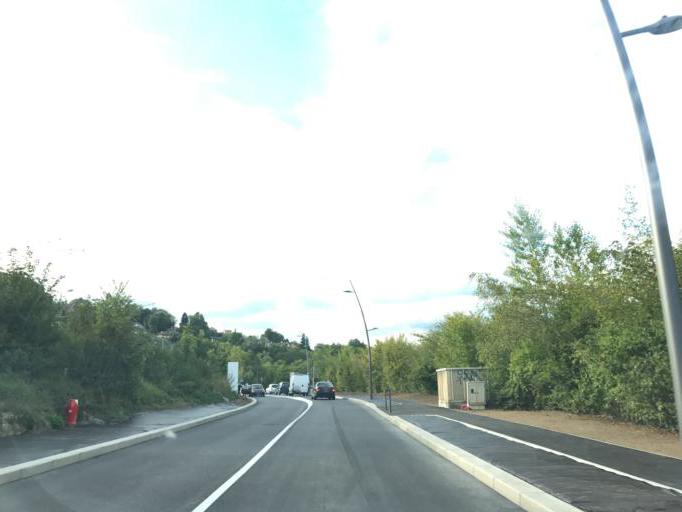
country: FR
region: Rhone-Alpes
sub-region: Departement de l'Ain
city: Bellegarde-sur-Valserine
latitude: 46.1135
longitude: 5.8256
